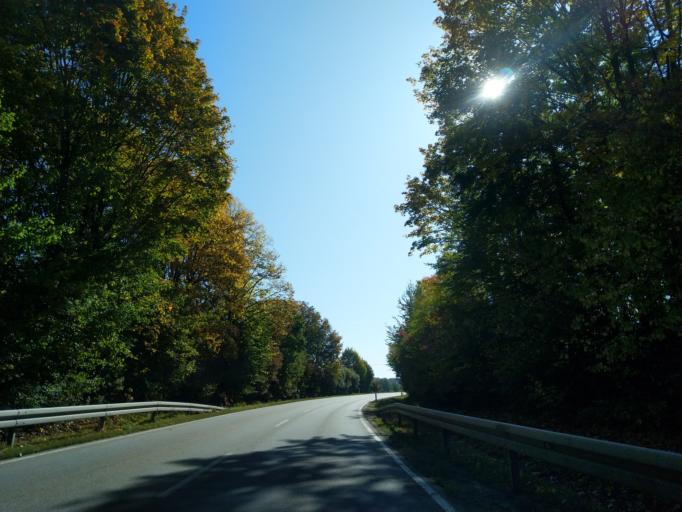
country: DE
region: Bavaria
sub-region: Lower Bavaria
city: Plattling
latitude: 48.8104
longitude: 12.9020
